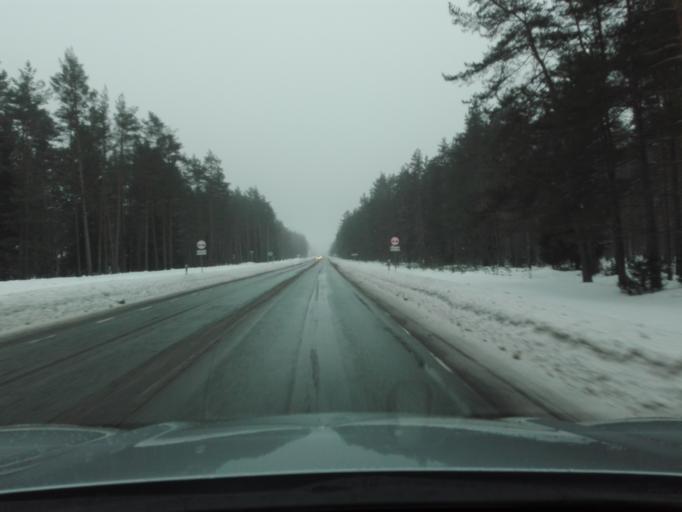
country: EE
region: Harju
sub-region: Kiili vald
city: Kiili
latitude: 59.3499
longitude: 24.7742
